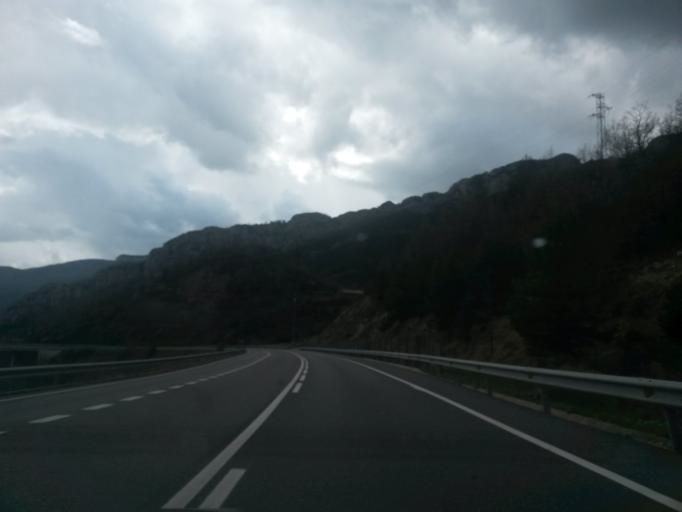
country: ES
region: Catalonia
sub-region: Provincia de Barcelona
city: Baga
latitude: 42.2867
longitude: 1.8513
